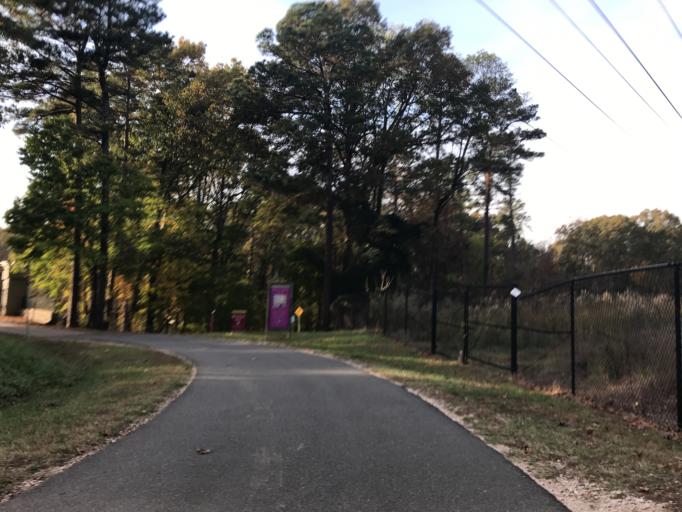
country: US
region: North Carolina
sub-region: Wake County
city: West Raleigh
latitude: 35.8055
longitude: -78.6921
